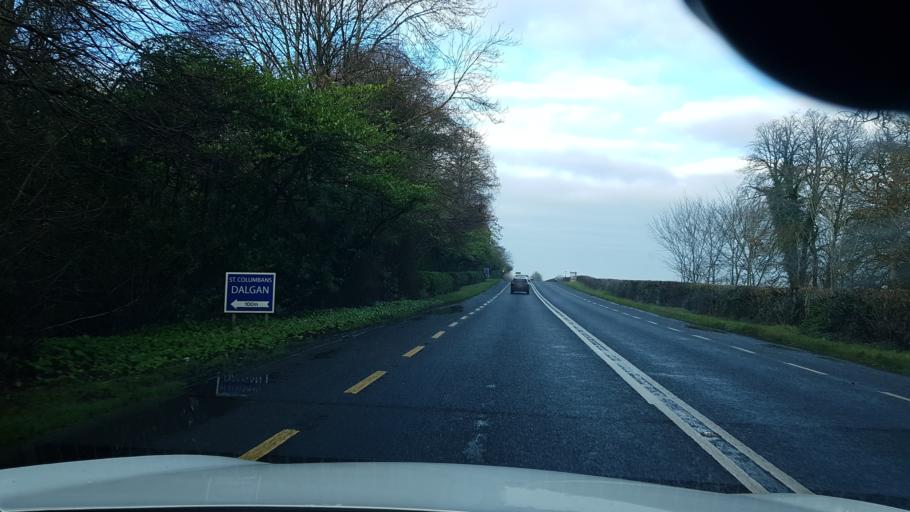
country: IE
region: Leinster
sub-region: An Mhi
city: Navan
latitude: 53.6072
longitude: -6.6252
